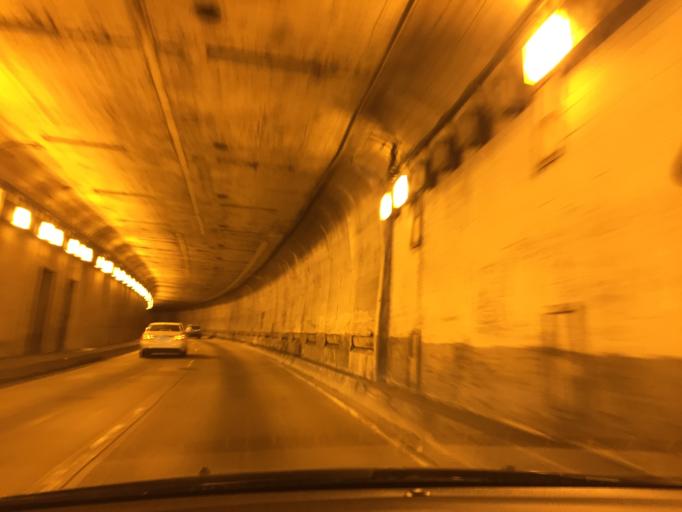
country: US
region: California
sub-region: Alameda County
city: Piedmont
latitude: 37.8548
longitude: -122.2167
